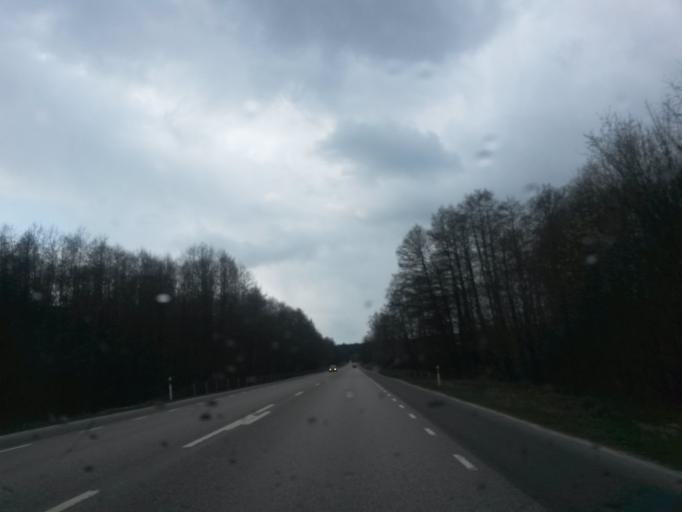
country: SE
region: Vaestra Goetaland
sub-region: Skovde Kommun
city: Skoevde
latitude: 58.3855
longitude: 13.8012
